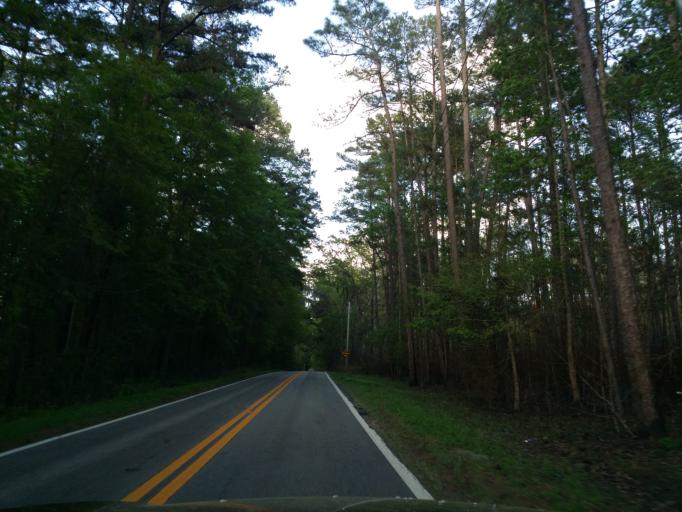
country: US
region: Florida
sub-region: Leon County
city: Tallahassee
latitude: 30.5084
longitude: -84.1485
